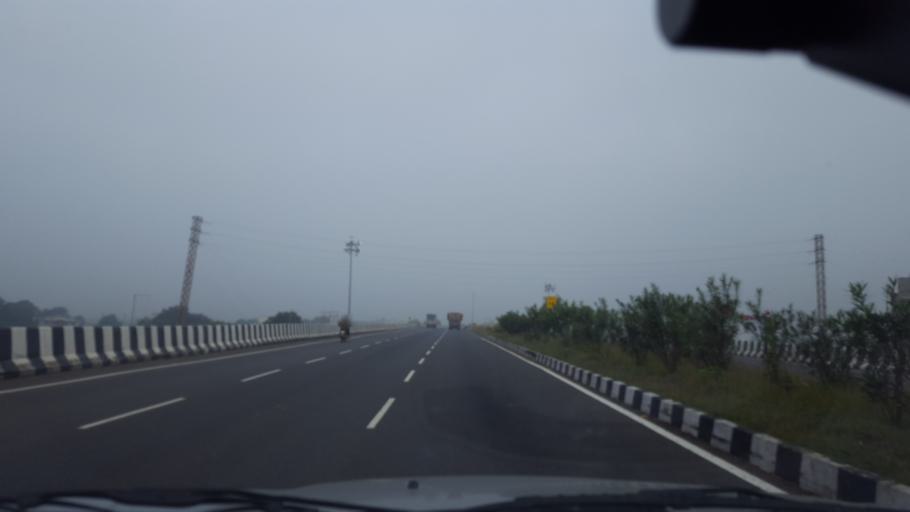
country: IN
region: Andhra Pradesh
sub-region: Prakasam
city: Ongole
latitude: 15.5318
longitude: 80.0530
